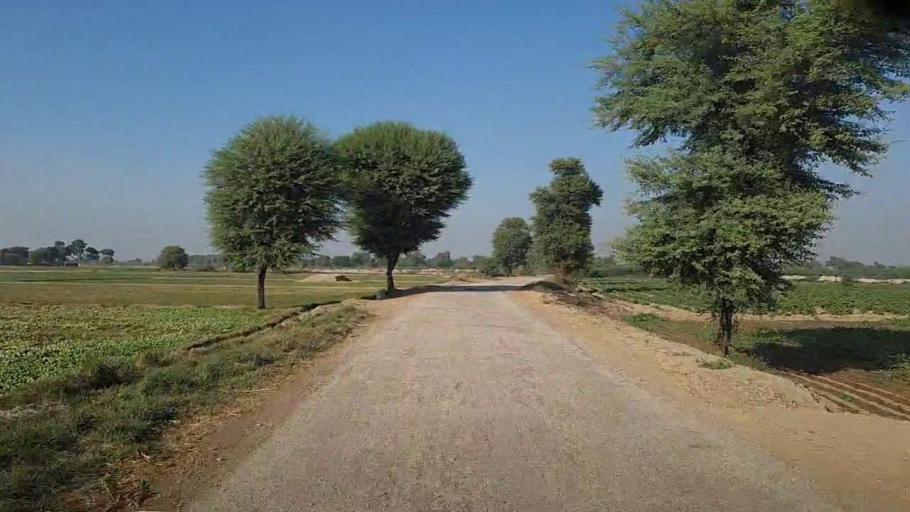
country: PK
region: Sindh
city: Darya Khan Marri
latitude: 26.6871
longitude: 68.3513
